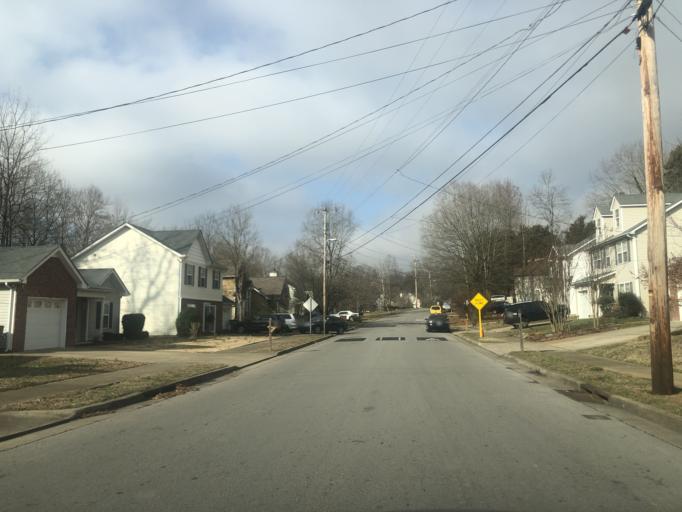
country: US
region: Tennessee
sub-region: Rutherford County
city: La Vergne
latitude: 36.0759
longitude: -86.6555
